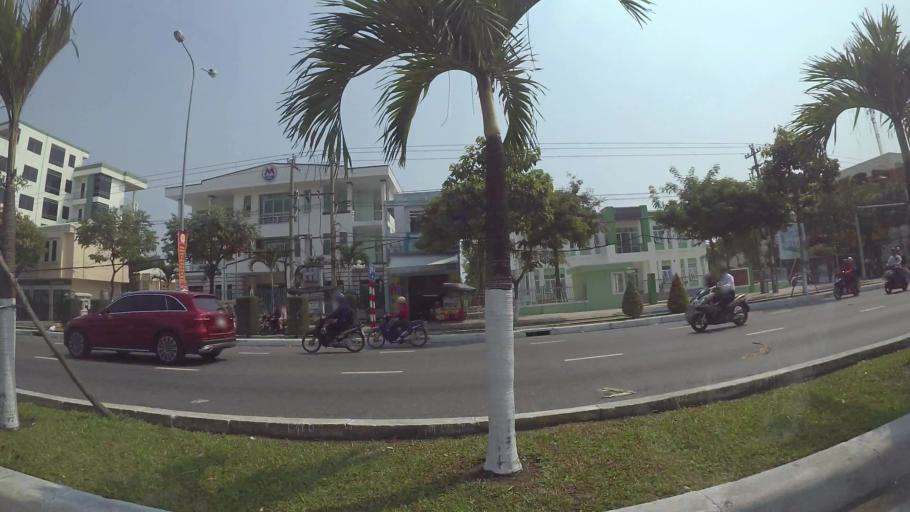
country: VN
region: Da Nang
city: Son Tra
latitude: 16.0423
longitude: 108.2409
